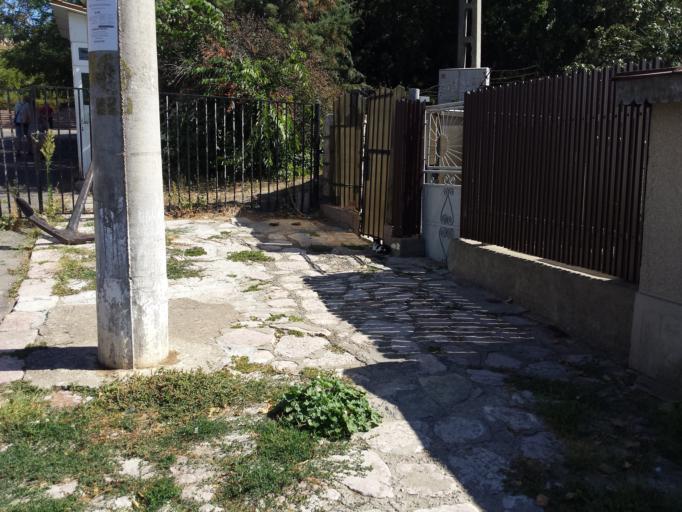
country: RO
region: Tulcea
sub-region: Municipiul Tulcea
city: Tulcea
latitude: 45.1857
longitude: 28.8138
